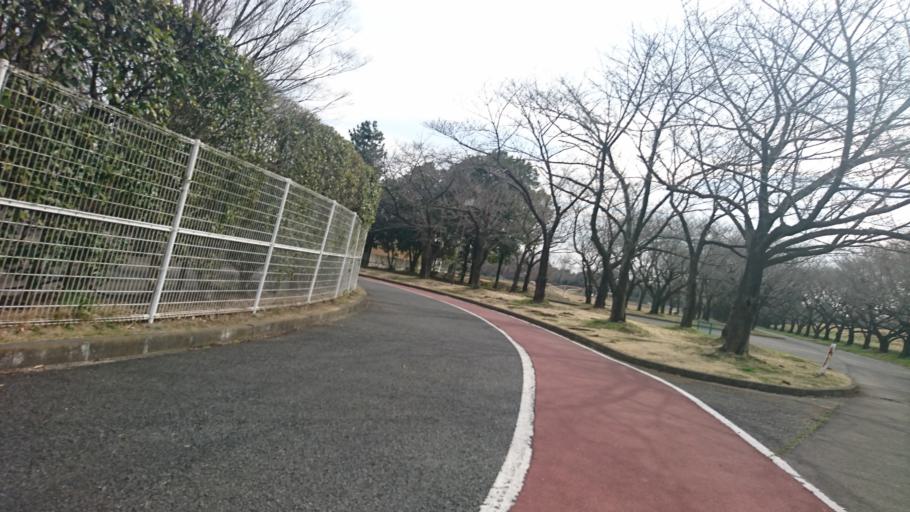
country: JP
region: Saitama
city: Kawagoe
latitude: 35.9121
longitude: 139.4468
